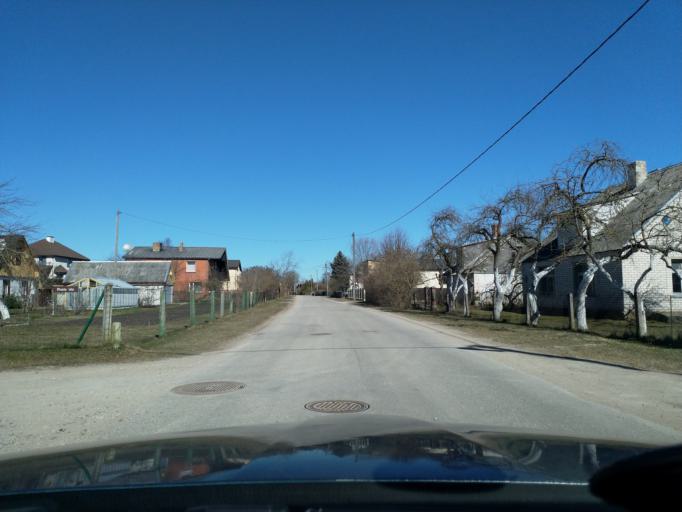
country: LV
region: Kuldigas Rajons
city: Kuldiga
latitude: 56.9613
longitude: 21.9987
